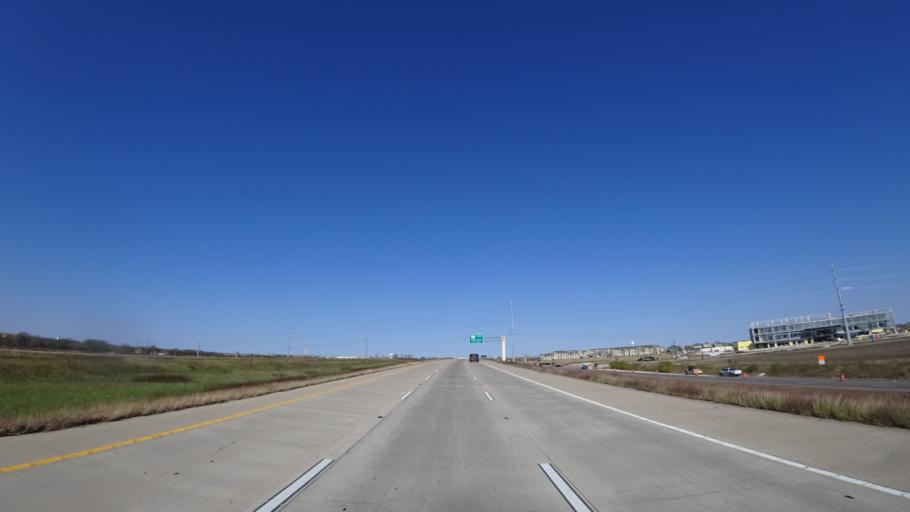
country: US
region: Texas
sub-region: Travis County
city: Pflugerville
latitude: 30.4492
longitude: -97.5939
